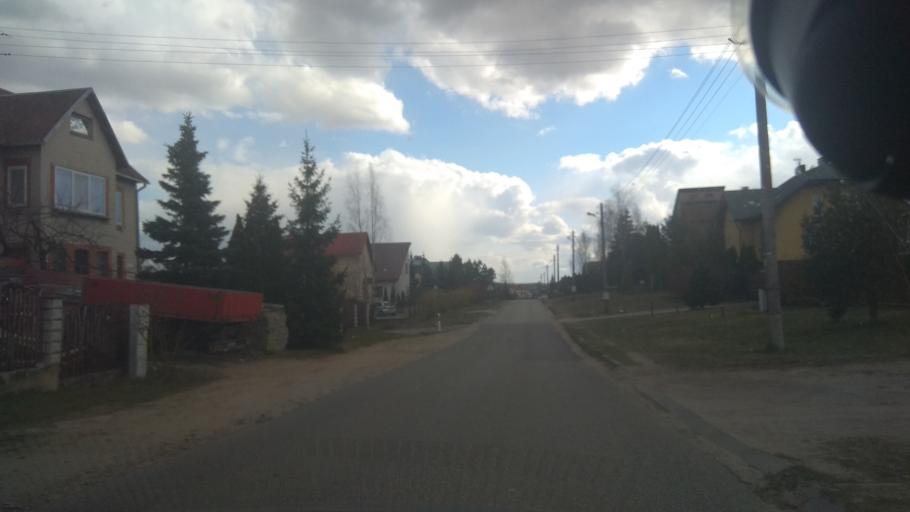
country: LT
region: Vilnius County
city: Pasilaiciai
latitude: 54.7397
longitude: 25.2022
